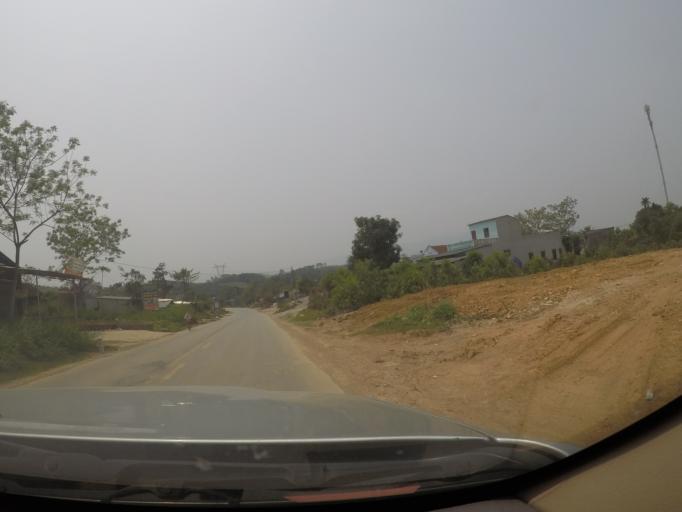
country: VN
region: Thanh Hoa
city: Thi Tran Thuong Xuan
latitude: 19.8331
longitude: 105.3931
